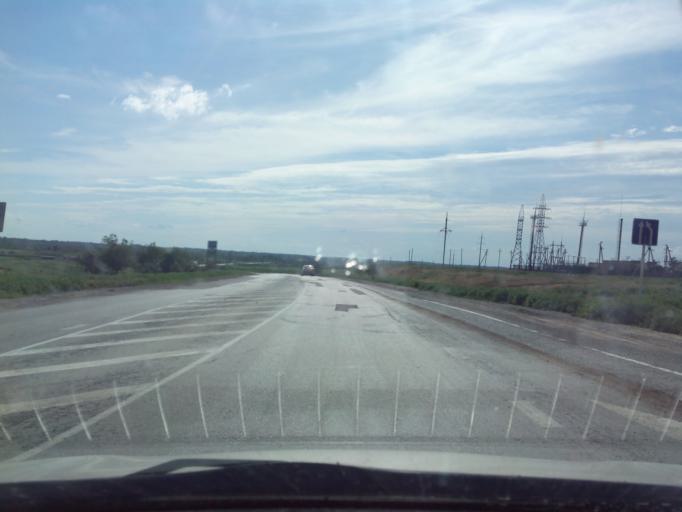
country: RU
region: Astrakhan
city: Kapustin Yar
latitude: 48.5648
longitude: 45.7858
